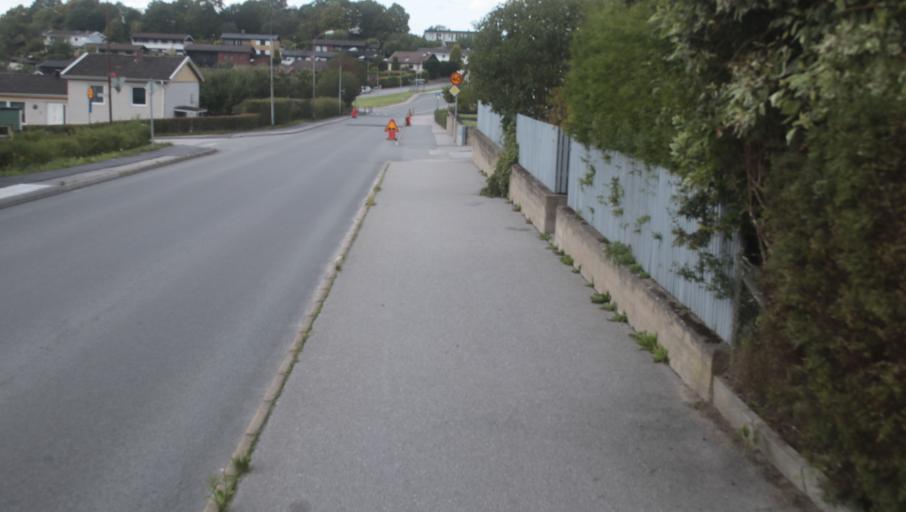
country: SE
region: Blekinge
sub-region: Karlshamns Kommun
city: Karlshamn
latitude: 56.1864
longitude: 14.8637
